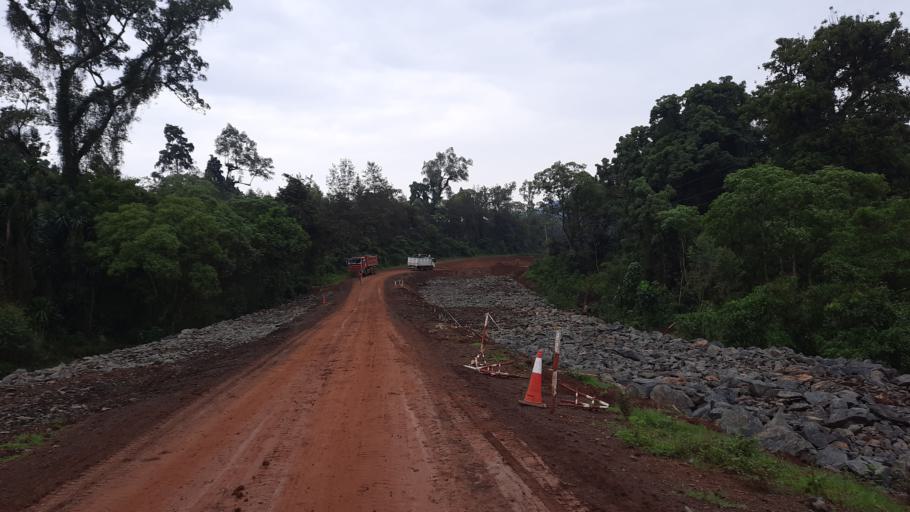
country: ET
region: Oromiya
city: Gore
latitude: 7.8625
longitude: 35.4778
